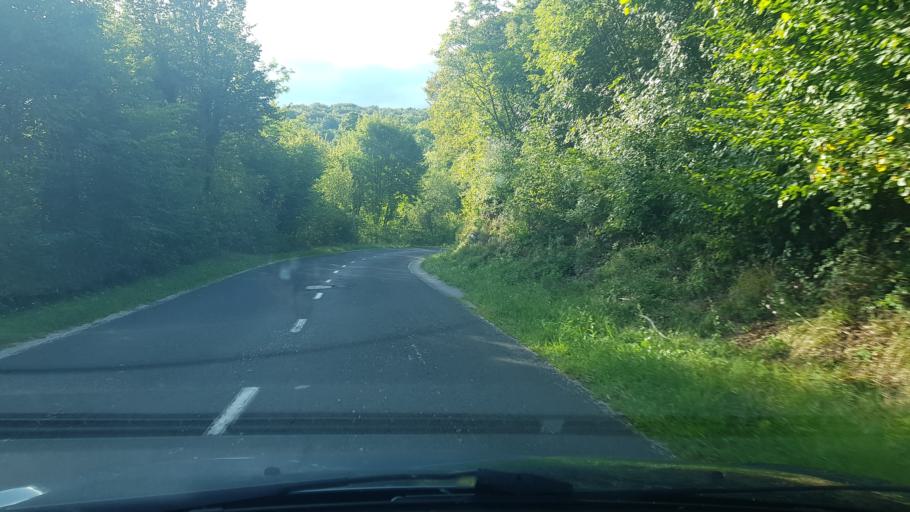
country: SI
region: Nova Gorica
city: Solkan
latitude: 46.0095
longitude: 13.6768
